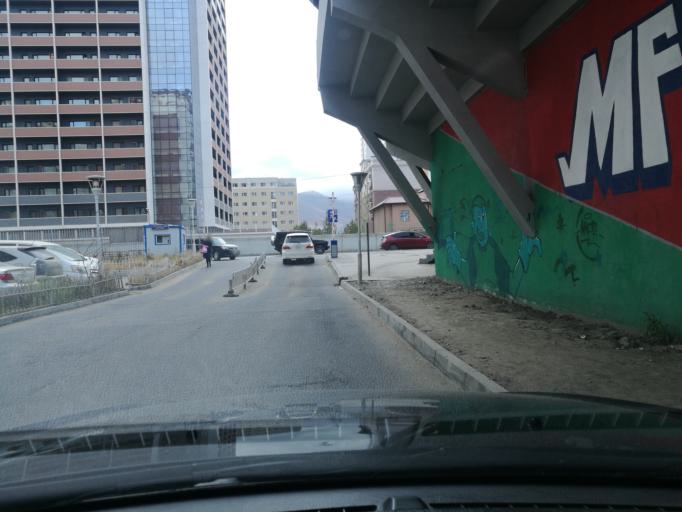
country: MN
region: Ulaanbaatar
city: Ulaanbaatar
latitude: 47.8999
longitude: 106.9172
